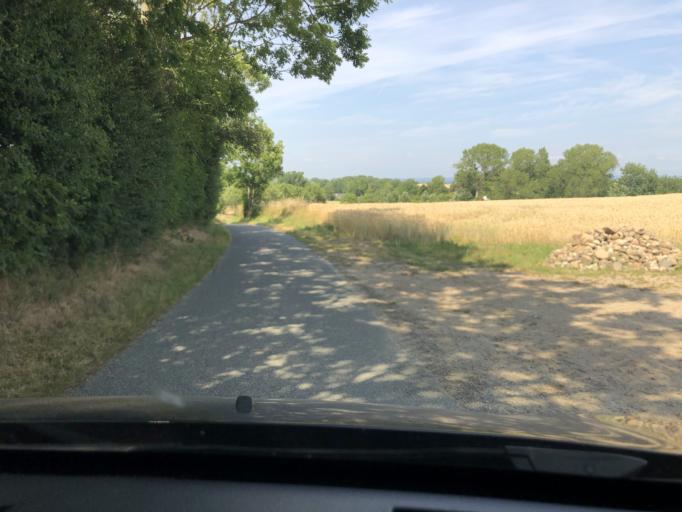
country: DK
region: South Denmark
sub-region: AEro Kommune
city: AEroskobing
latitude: 54.9097
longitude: 10.2965
